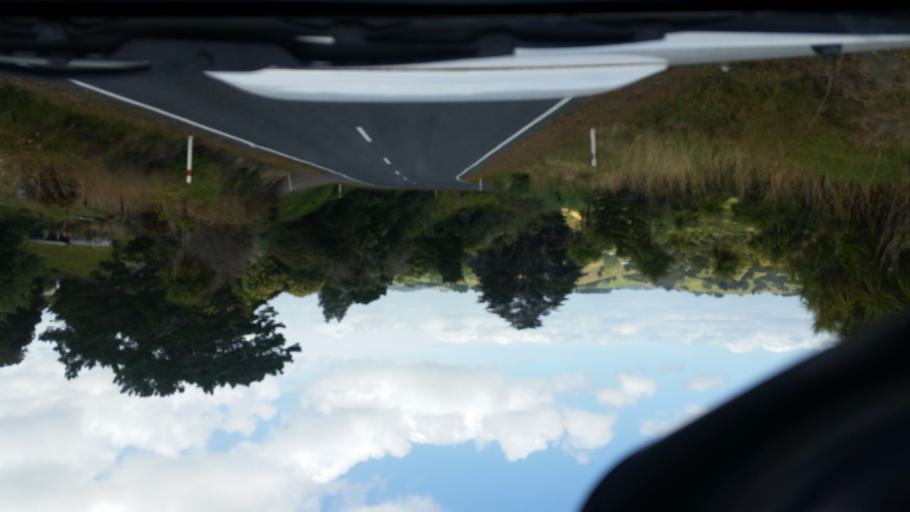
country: NZ
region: Northland
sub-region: Whangarei
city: Ruakaka
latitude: -36.0894
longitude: 174.2401
